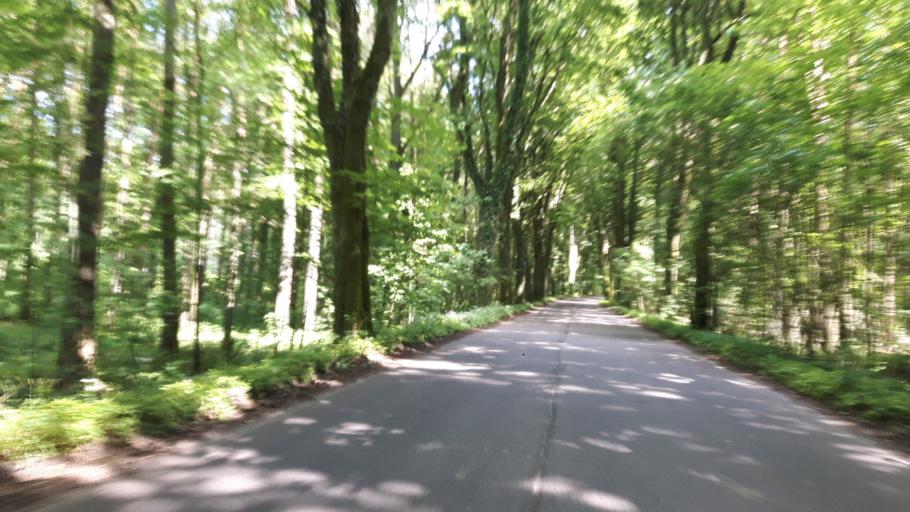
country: PL
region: West Pomeranian Voivodeship
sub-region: Powiat goleniowski
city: Nowogard
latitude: 53.6710
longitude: 15.0869
